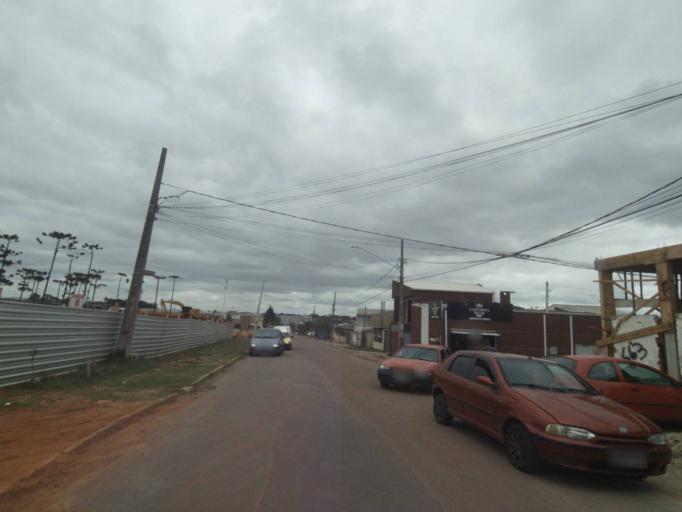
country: BR
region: Parana
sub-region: Sao Jose Dos Pinhais
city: Sao Jose dos Pinhais
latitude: -25.5586
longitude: -49.2642
